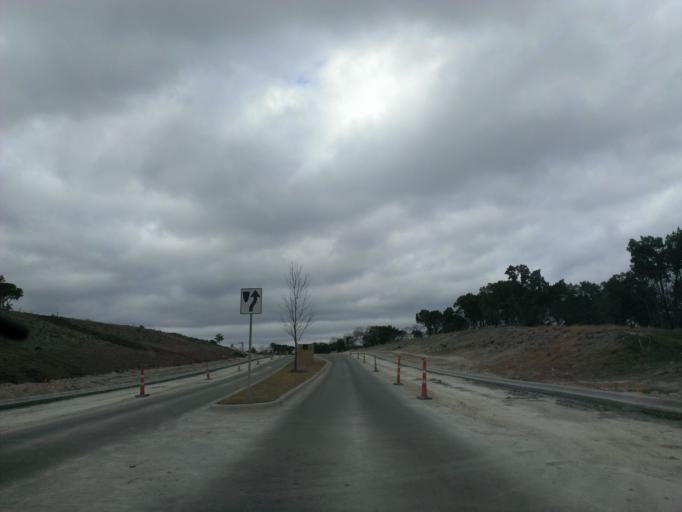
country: US
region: Texas
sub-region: Travis County
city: The Hills
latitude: 30.3459
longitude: -98.0204
